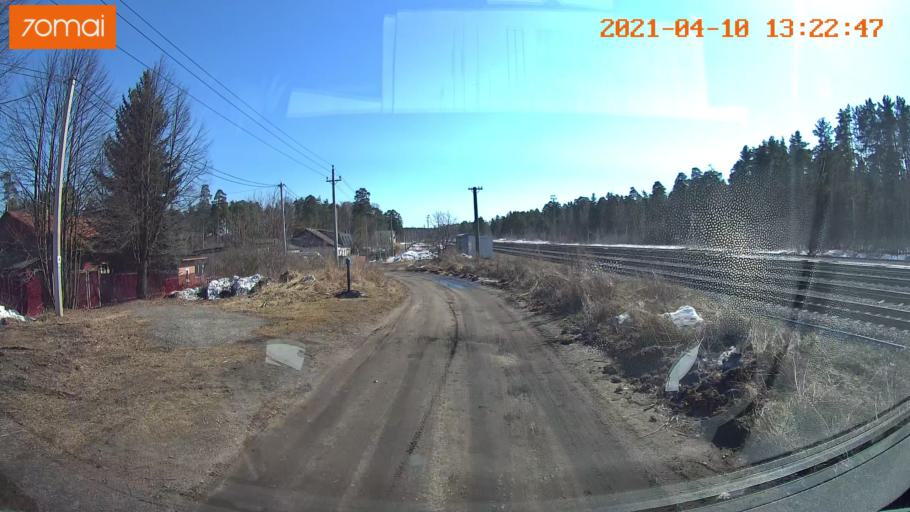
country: RU
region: Ivanovo
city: Kokhma
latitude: 56.9852
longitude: 41.0616
